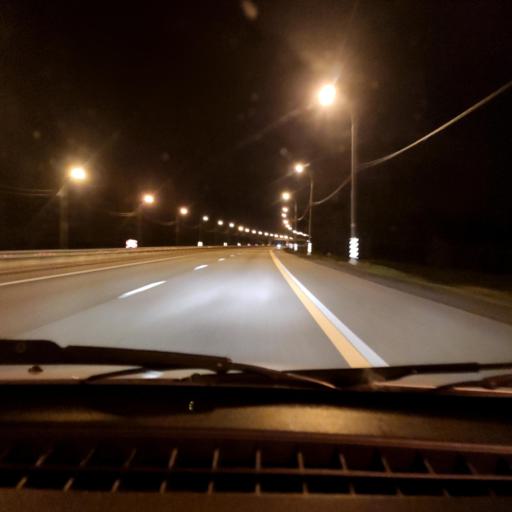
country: RU
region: Lipetsk
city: Zadonsk
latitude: 52.3828
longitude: 38.8742
